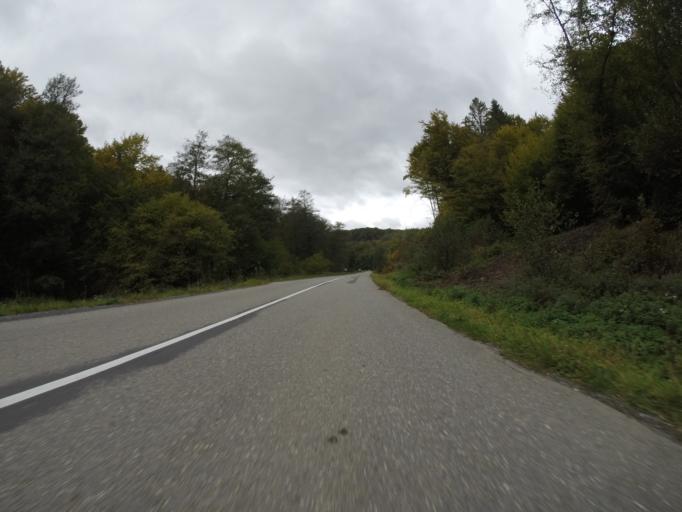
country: SK
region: Banskobystricky
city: Poltar
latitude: 48.5903
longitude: 19.7879
